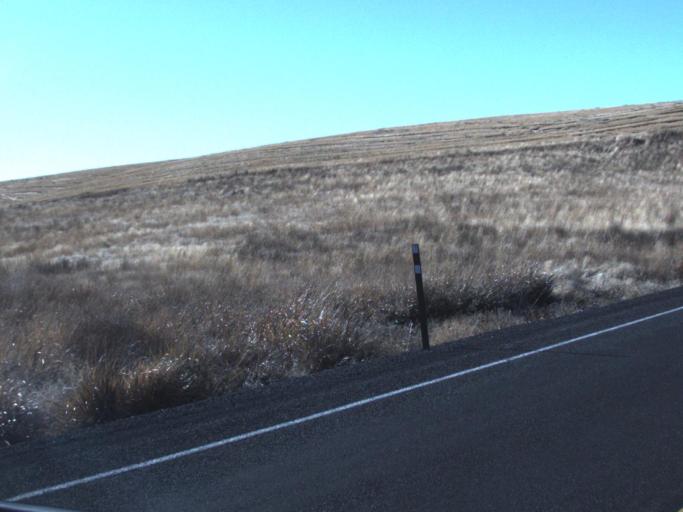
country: US
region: Washington
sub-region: Adams County
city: Ritzville
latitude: 46.8214
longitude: -118.3200
